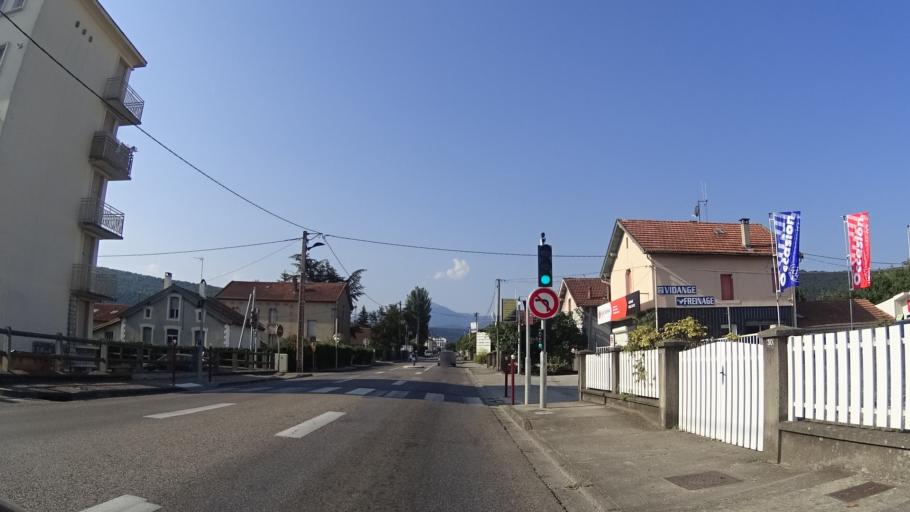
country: FR
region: Midi-Pyrenees
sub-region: Departement de l'Ariege
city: Lavelanet
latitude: 42.9679
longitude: 1.8657
